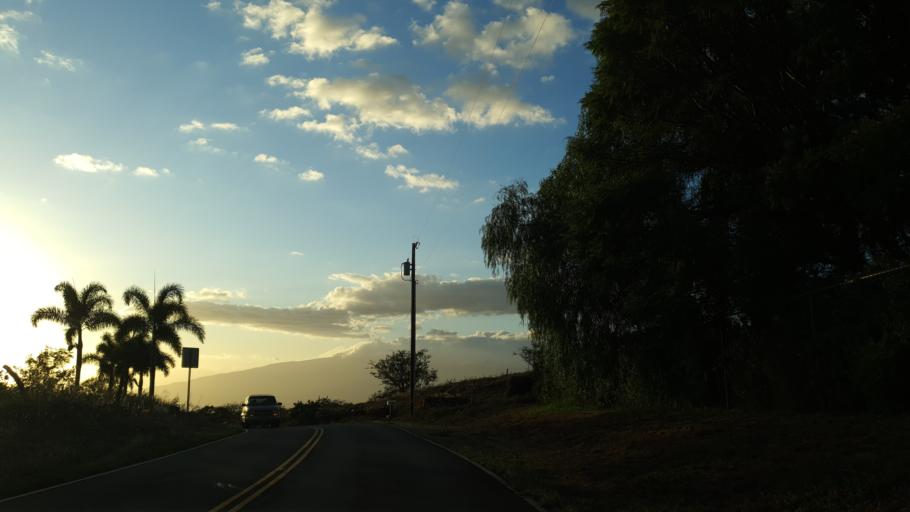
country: US
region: Hawaii
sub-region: Maui County
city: Pukalani
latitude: 20.7835
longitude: -156.3434
